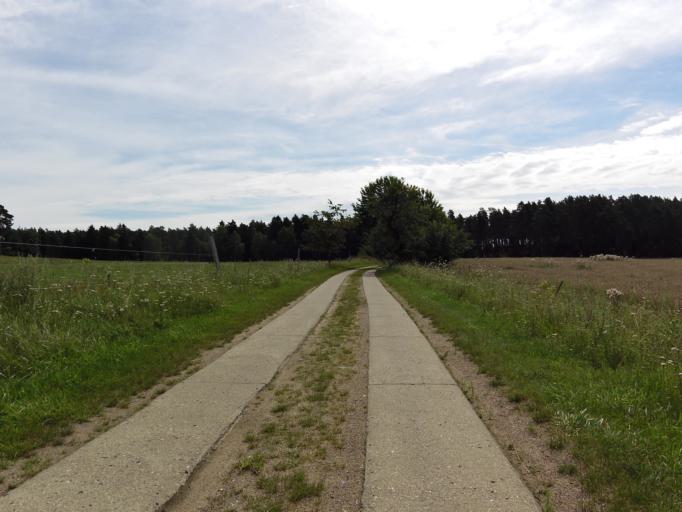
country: DE
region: Brandenburg
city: Lychen
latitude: 53.2837
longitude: 13.3600
